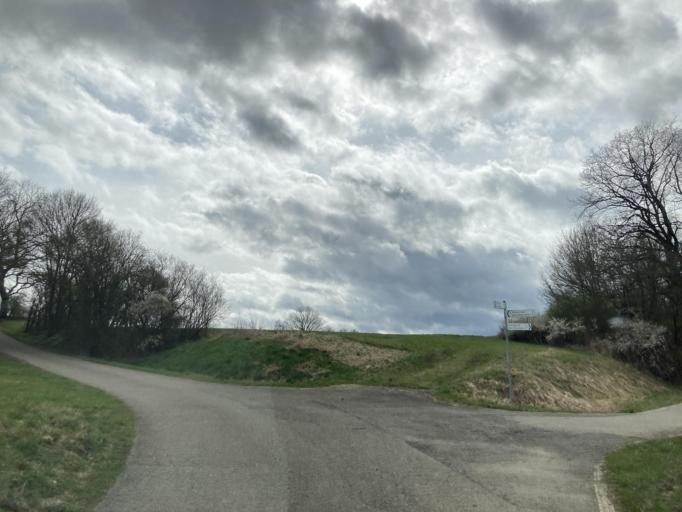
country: DE
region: Baden-Wuerttemberg
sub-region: Tuebingen Region
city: Gomaringen
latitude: 48.4692
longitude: 9.1001
